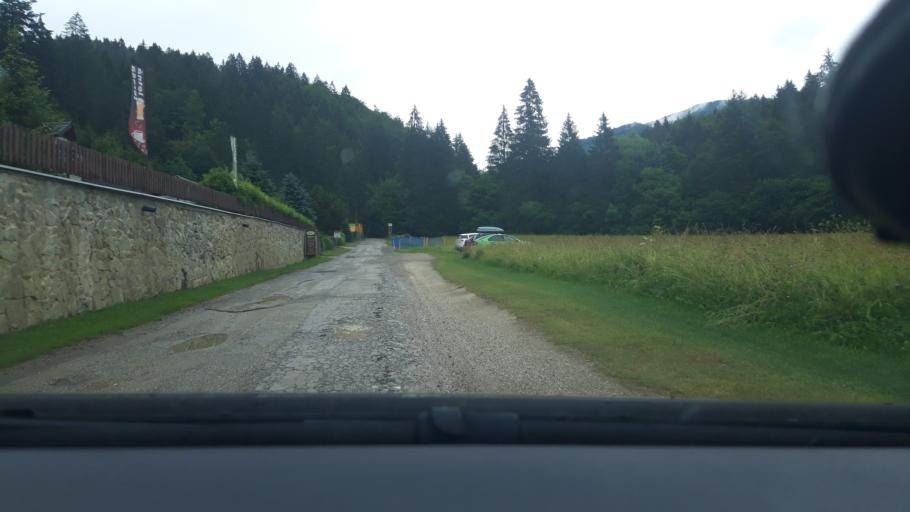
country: SK
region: Zilinsky
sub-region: Okres Martin
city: Martin
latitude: 49.0136
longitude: 19.0145
